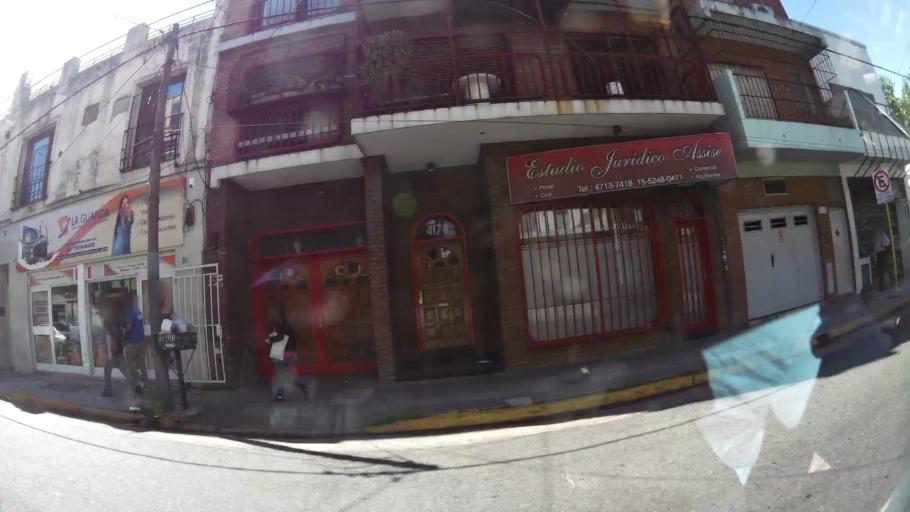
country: AR
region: Buenos Aires
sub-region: Partido de General San Martin
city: General San Martin
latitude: -34.5795
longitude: -58.5416
